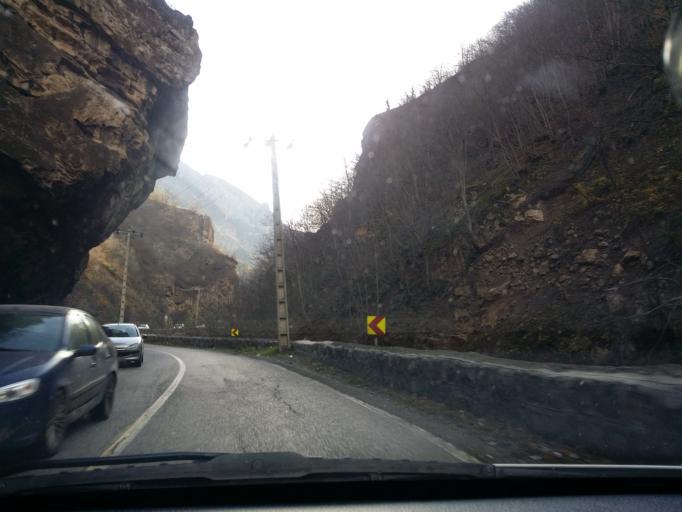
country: IR
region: Mazandaran
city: Chalus
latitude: 36.2696
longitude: 51.2493
